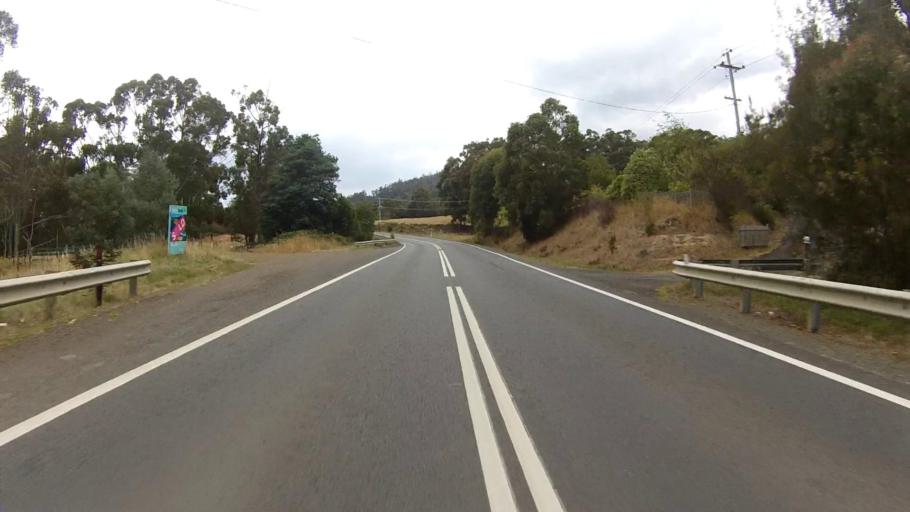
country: AU
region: Tasmania
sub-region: Huon Valley
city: Huonville
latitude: -43.0540
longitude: 147.0483
